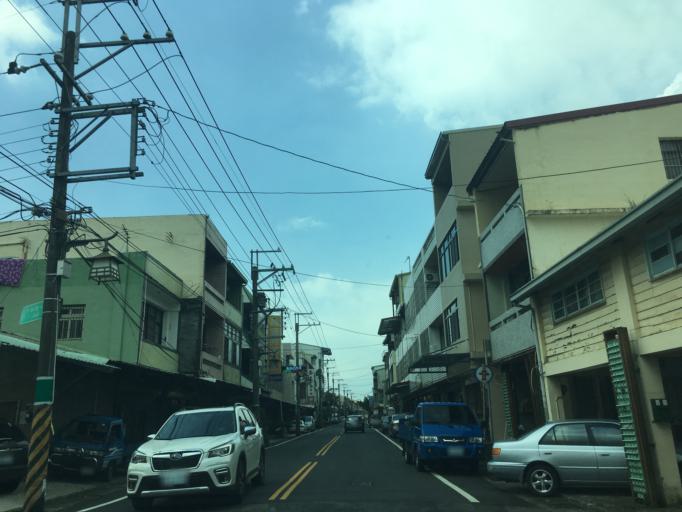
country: TW
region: Taiwan
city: Fengyuan
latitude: 24.2195
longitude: 120.7931
